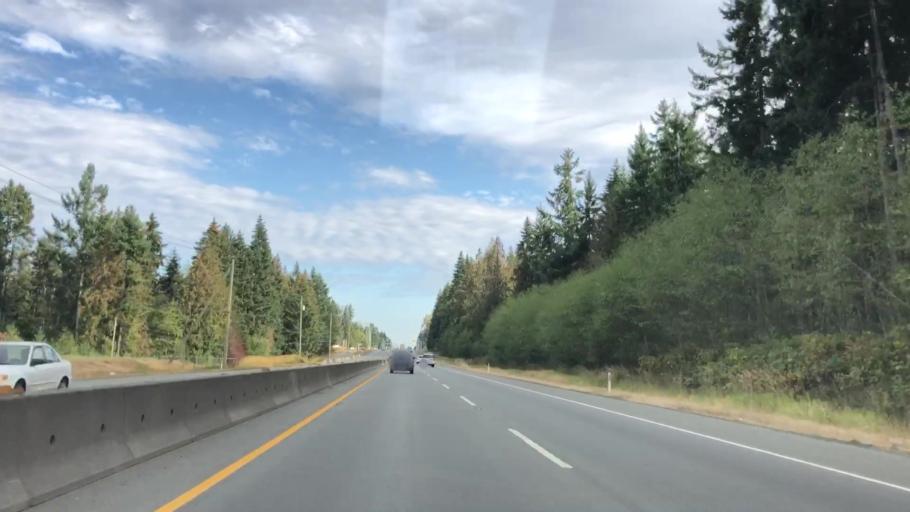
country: CA
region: British Columbia
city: Duncan
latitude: 48.7007
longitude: -123.5983
